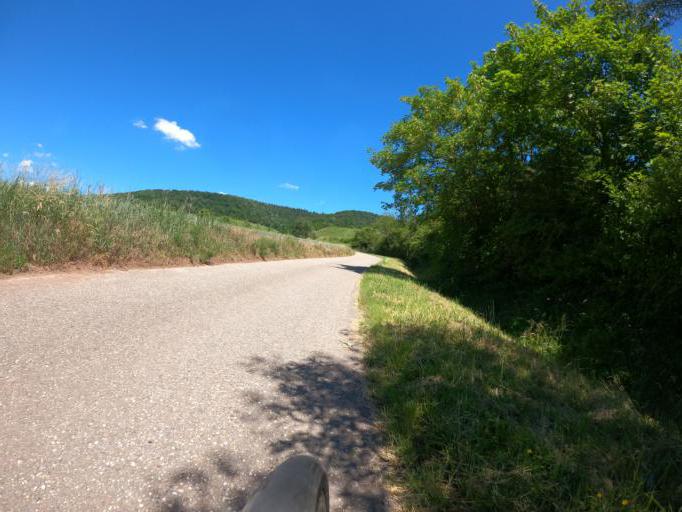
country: DE
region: Baden-Wuerttemberg
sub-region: Regierungsbezirk Stuttgart
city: Sersheim
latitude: 49.0021
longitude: 9.0210
